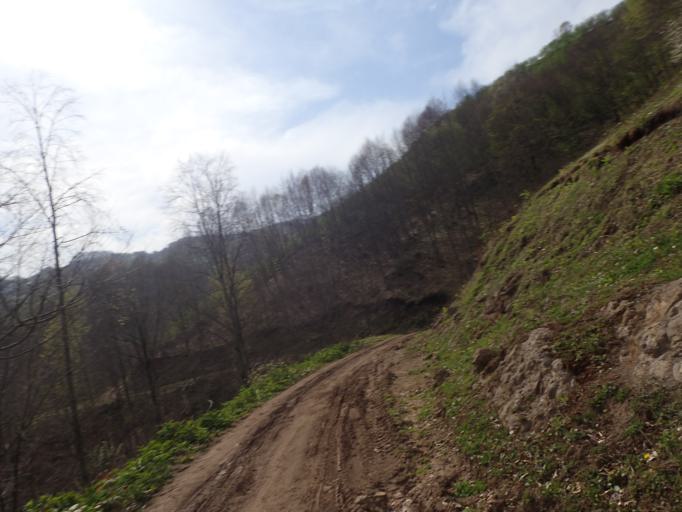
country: TR
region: Ordu
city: Aybasti
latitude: 40.7211
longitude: 37.2956
